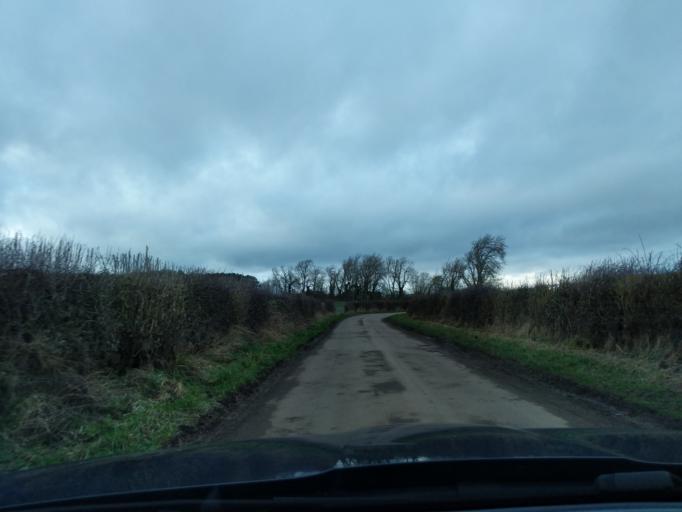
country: GB
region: England
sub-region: Northumberland
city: Ancroft
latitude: 55.7034
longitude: -2.0257
